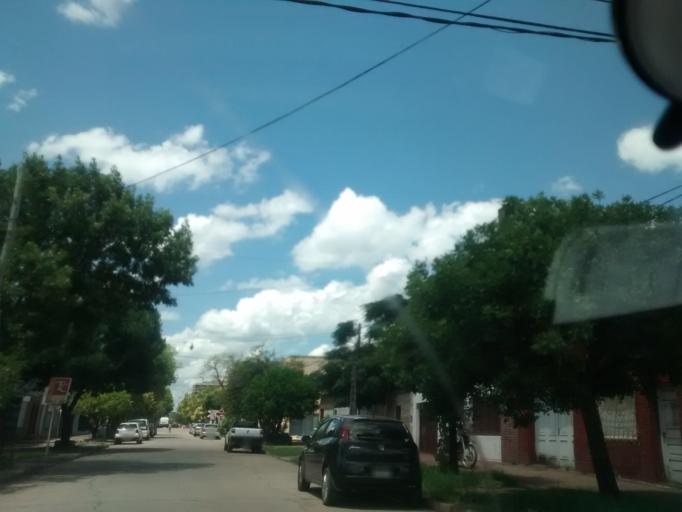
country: AR
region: Chaco
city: Resistencia
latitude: -27.4566
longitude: -58.9908
